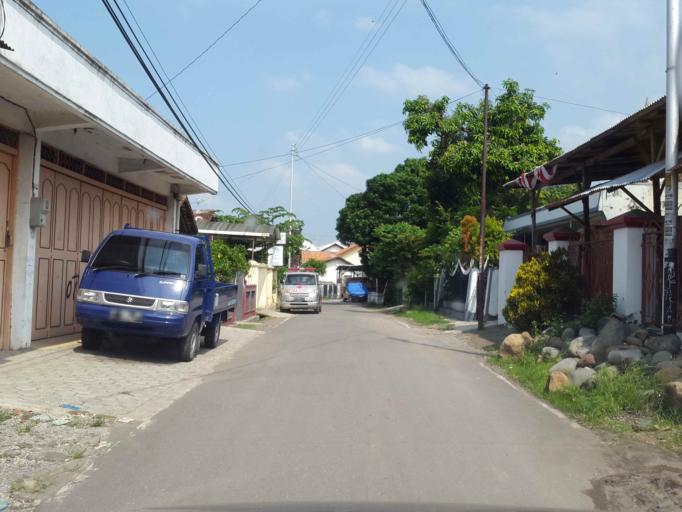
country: ID
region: Central Java
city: Balapulang
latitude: -7.0528
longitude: 109.0988
